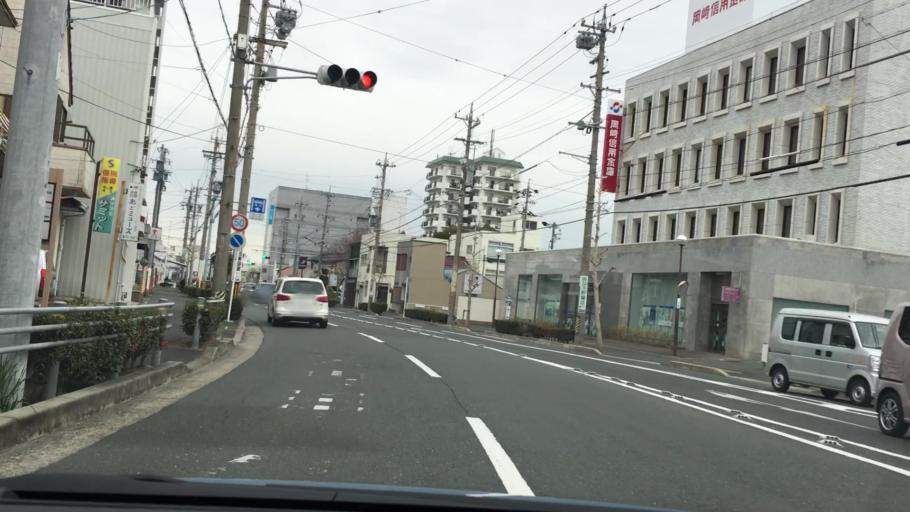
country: JP
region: Aichi
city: Toyohashi
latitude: 34.7608
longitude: 137.3978
